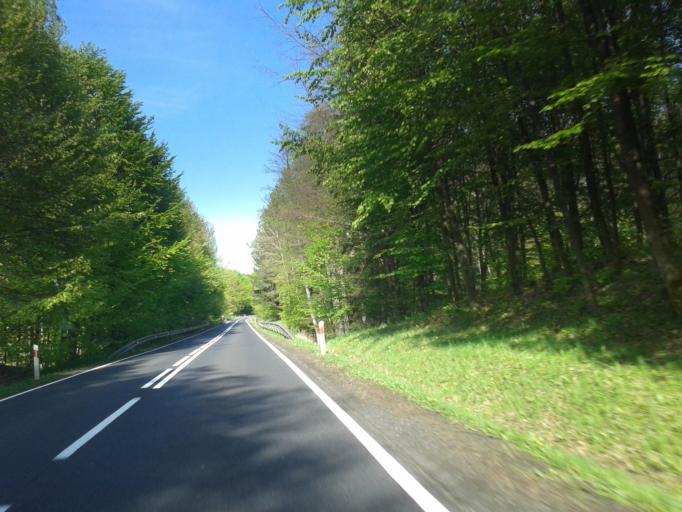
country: PL
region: West Pomeranian Voivodeship
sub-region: Powiat drawski
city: Czaplinek
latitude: 53.5887
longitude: 16.2953
